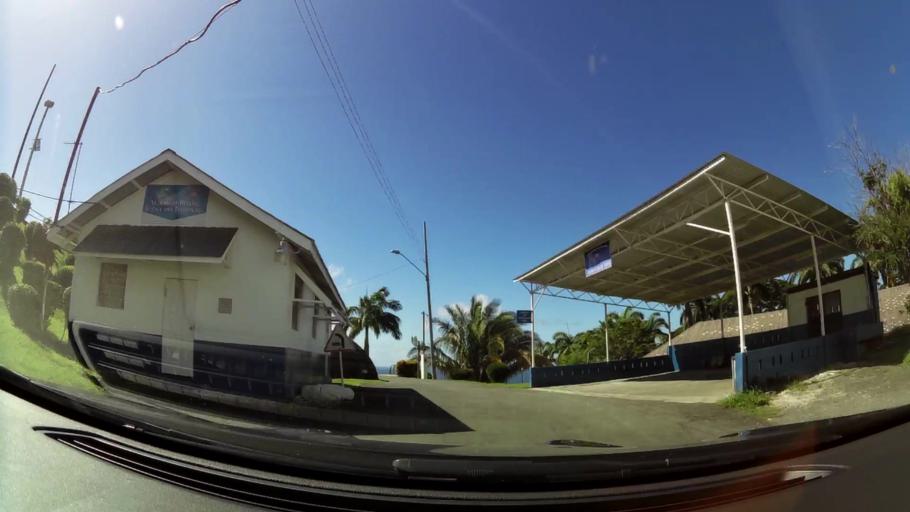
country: TT
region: Tobago
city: Scarborough
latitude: 11.1780
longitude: -60.7272
